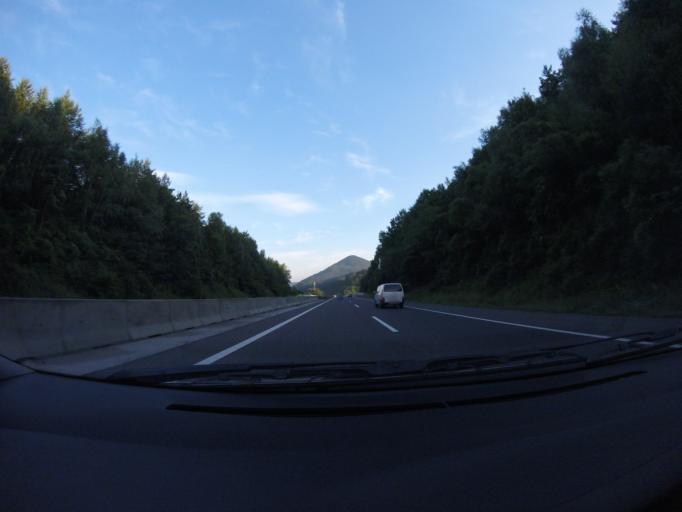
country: AT
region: Lower Austria
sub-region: Politischer Bezirk Neunkirchen
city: Warth
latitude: 47.6557
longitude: 16.1244
